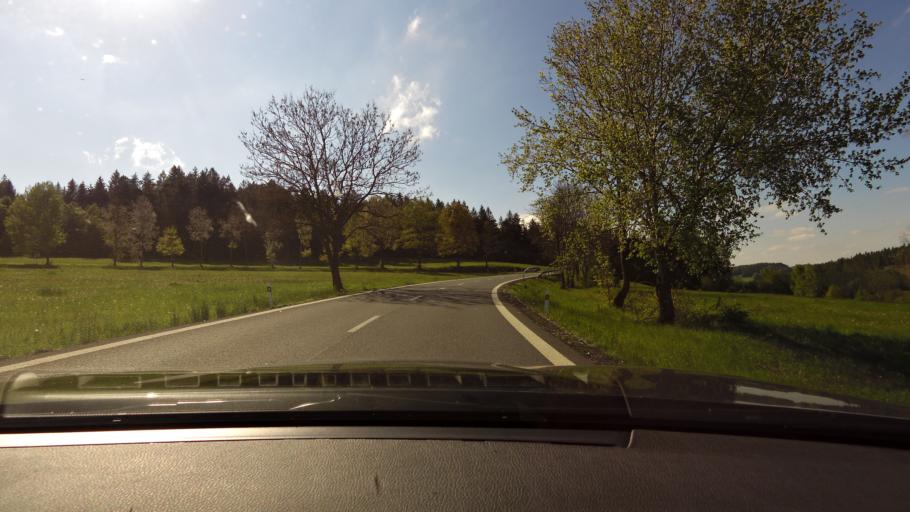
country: CZ
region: Plzensky
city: Strazov
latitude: 49.2812
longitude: 13.2909
